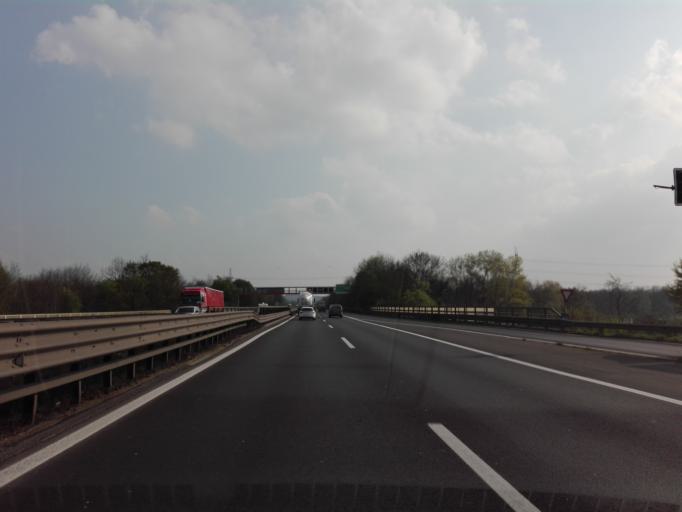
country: AT
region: Upper Austria
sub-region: Politischer Bezirk Linz-Land
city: Ansfelden
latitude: 48.2410
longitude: 14.2977
